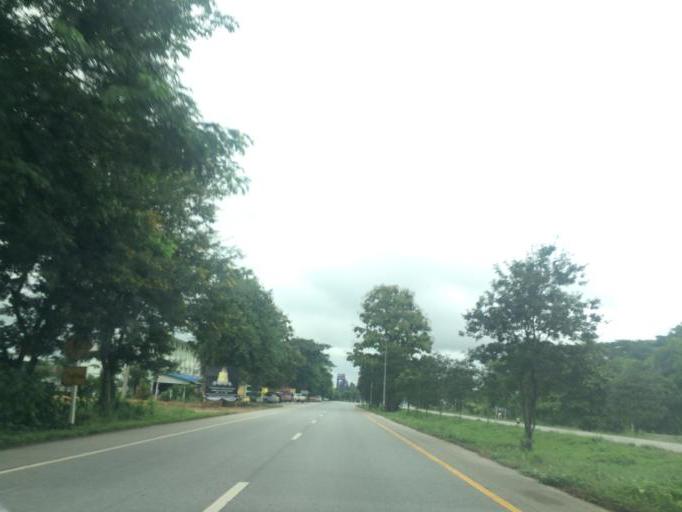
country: TH
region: Chiang Rai
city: Mae Lao
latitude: 19.8143
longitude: 99.7585
